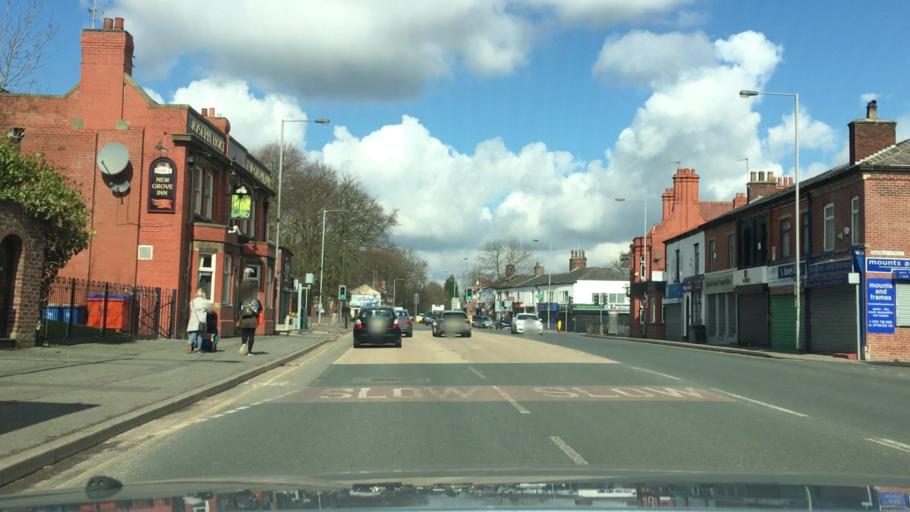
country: GB
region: England
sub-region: Borough of Bury
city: Whitefield
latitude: 53.5471
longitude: -2.2929
